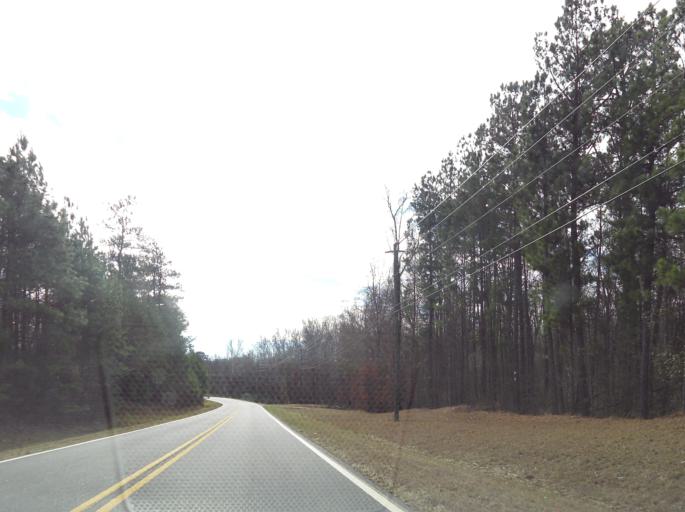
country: US
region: Georgia
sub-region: Bibb County
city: West Point
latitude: 32.8696
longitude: -83.7826
